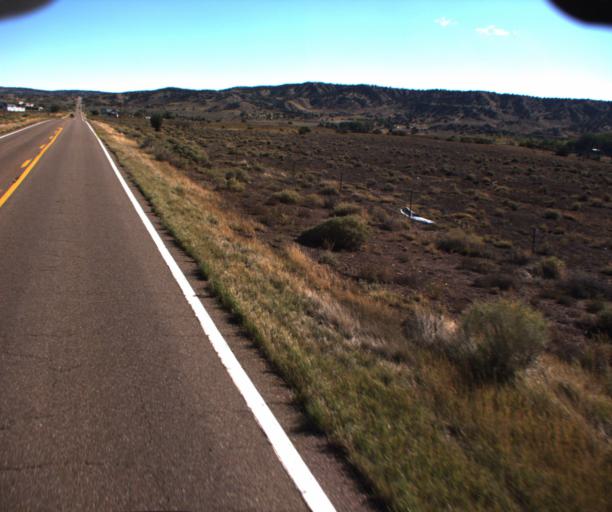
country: US
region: Arizona
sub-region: Apache County
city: Saint Johns
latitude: 34.4701
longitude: -109.6125
